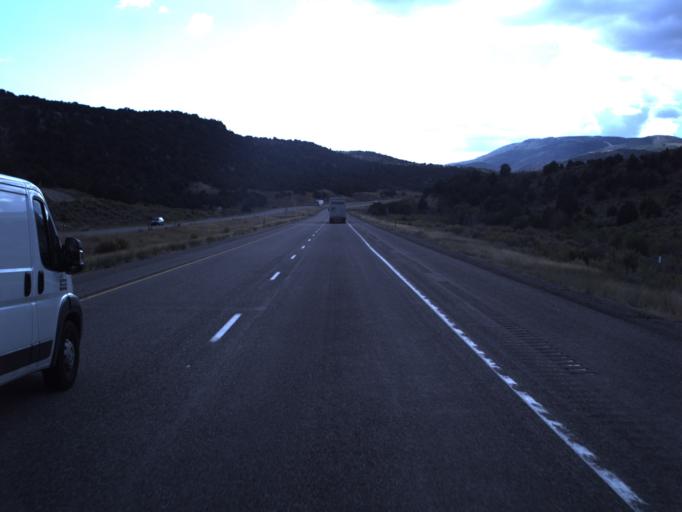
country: US
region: Utah
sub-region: Sevier County
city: Salina
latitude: 38.8456
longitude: -111.5398
